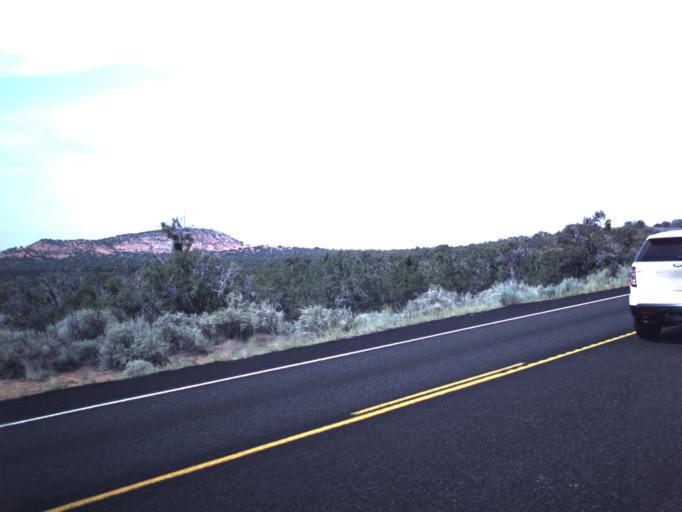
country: US
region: Utah
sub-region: Kane County
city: Kanab
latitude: 37.1655
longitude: -112.5999
